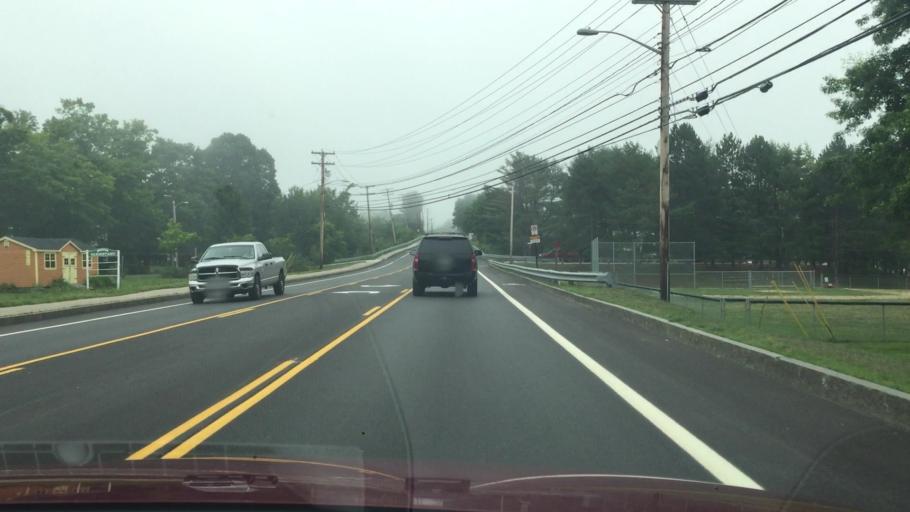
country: US
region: Maine
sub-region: Cumberland County
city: Freeport
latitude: 43.8502
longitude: -70.1108
